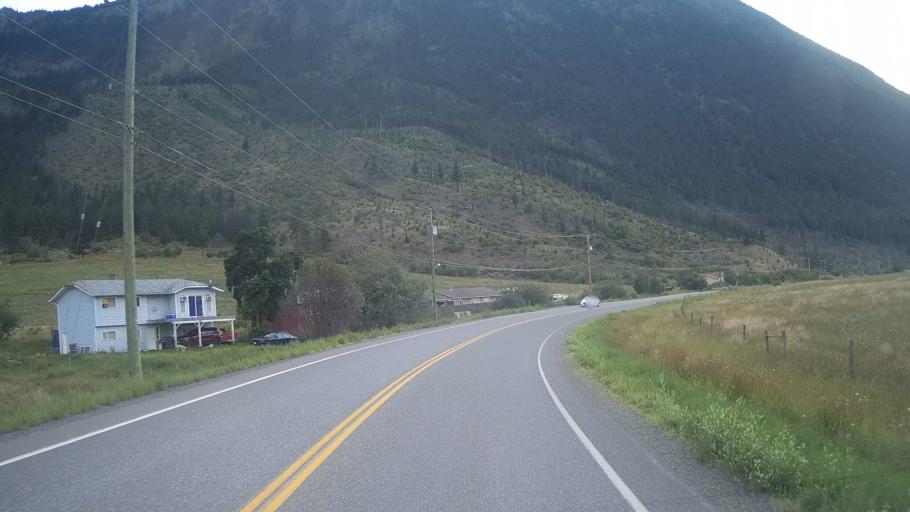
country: CA
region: British Columbia
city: Lillooet
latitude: 50.7420
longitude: -121.8826
